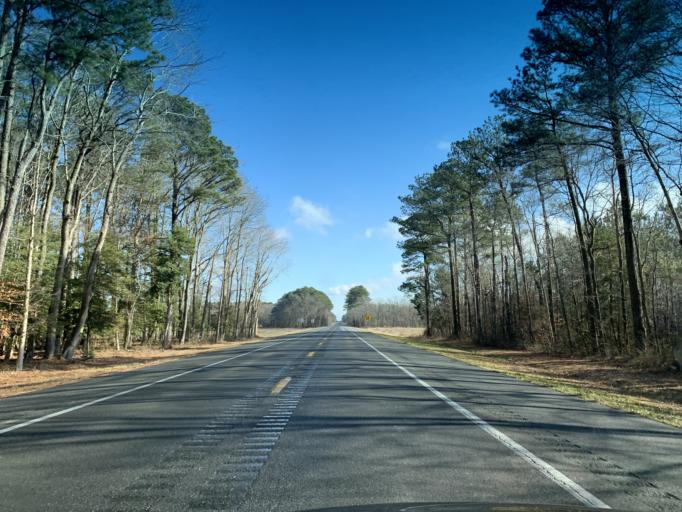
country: US
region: Maryland
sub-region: Worcester County
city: Berlin
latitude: 38.3771
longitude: -75.2290
